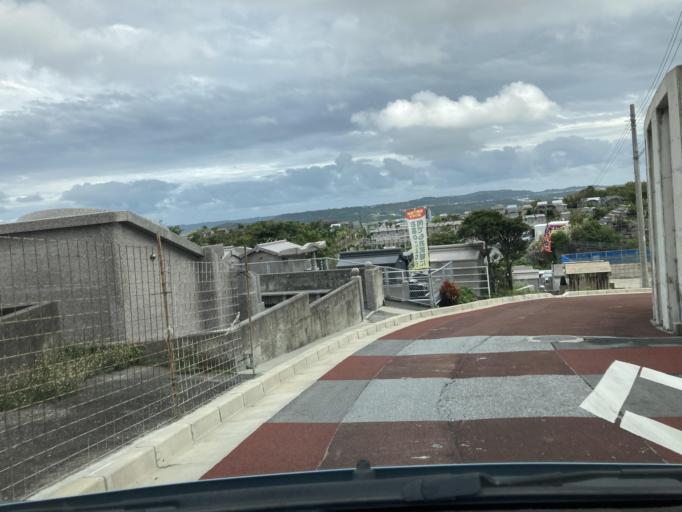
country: JP
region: Okinawa
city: Ginowan
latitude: 26.2171
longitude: 127.7345
